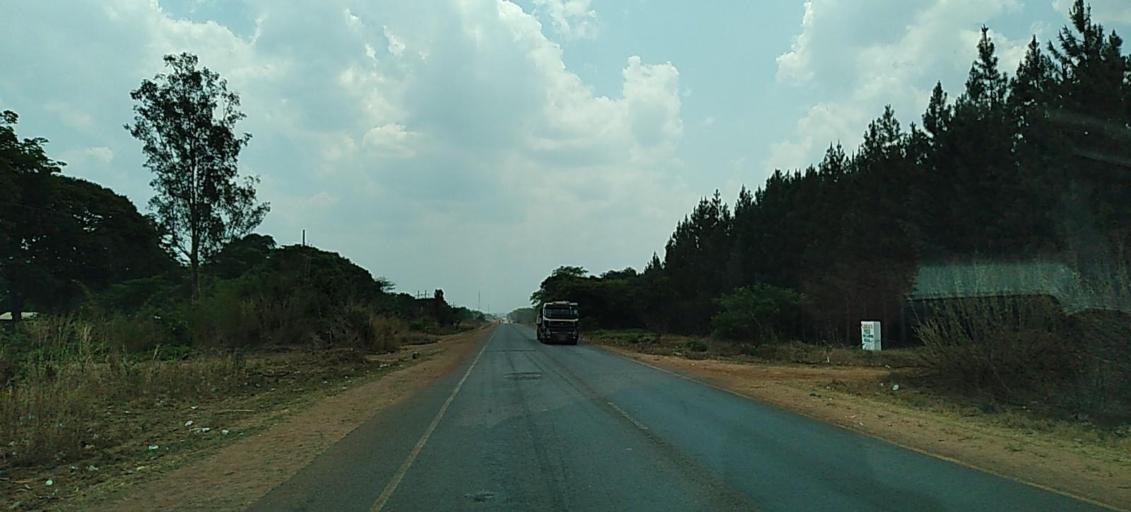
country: ZM
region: Copperbelt
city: Kalulushi
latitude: -12.8432
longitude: 28.0089
